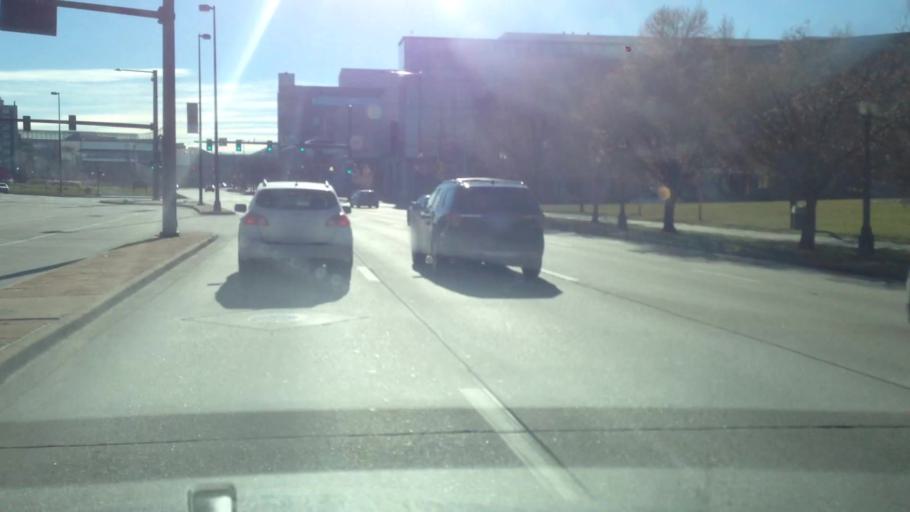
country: US
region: Colorado
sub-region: Denver County
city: Denver
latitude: 39.7484
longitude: -105.0033
